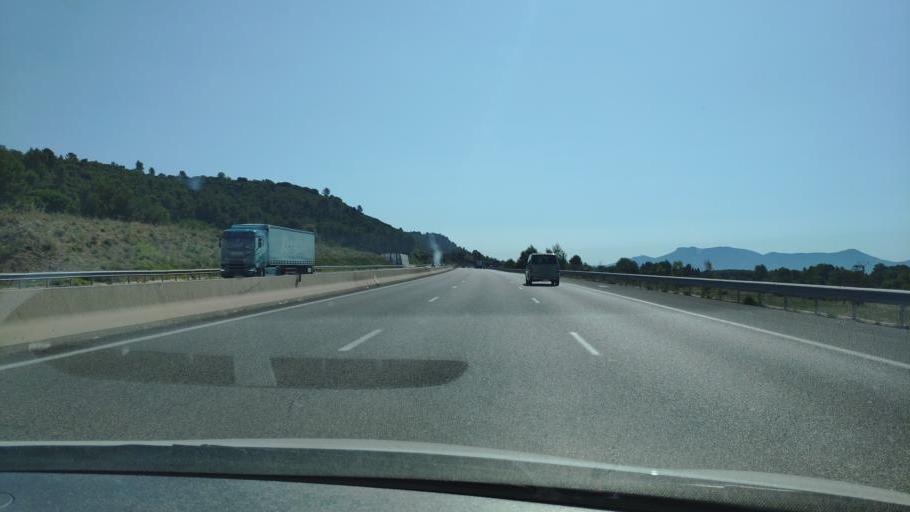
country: FR
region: Provence-Alpes-Cote d'Azur
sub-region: Departement des Bouches-du-Rhone
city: Chateauneuf-le-Rouge
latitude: 43.4788
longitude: 5.5838
